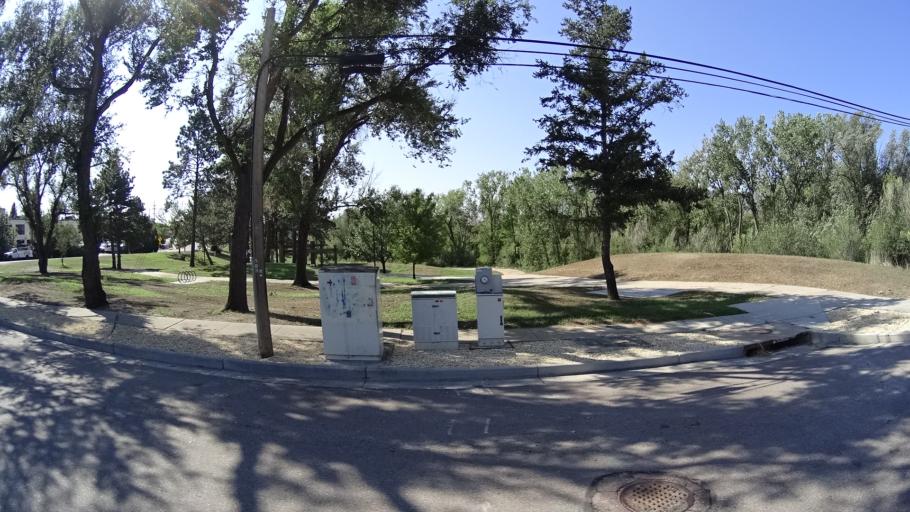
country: US
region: Colorado
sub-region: El Paso County
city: Colorado Springs
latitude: 38.8215
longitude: -104.8170
